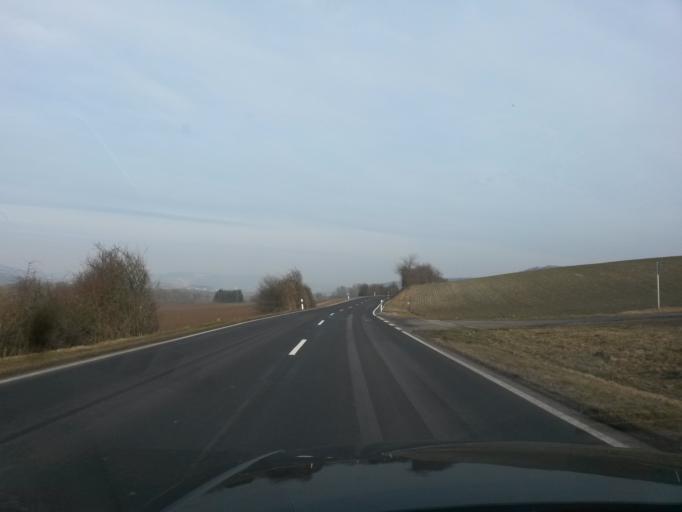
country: DE
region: Bavaria
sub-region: Regierungsbezirk Unterfranken
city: Sondheim vor der Rhoen
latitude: 50.4943
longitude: 10.1755
